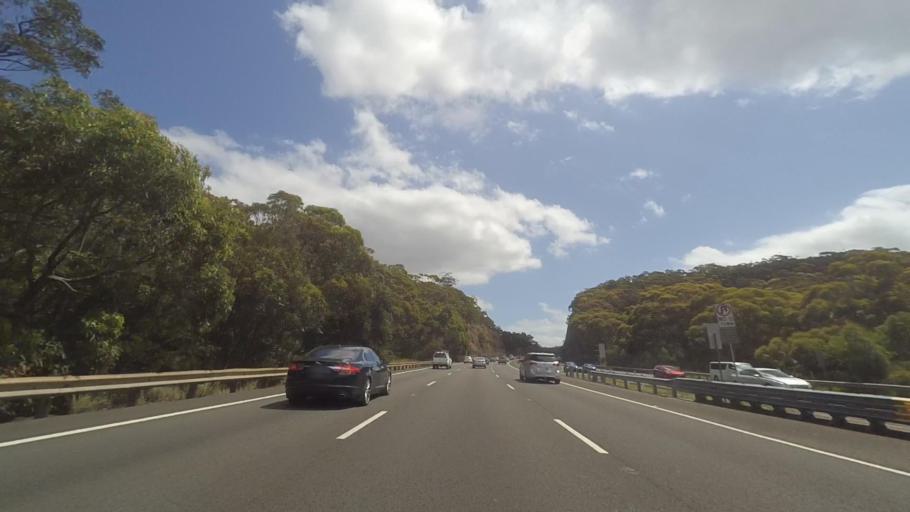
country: AU
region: New South Wales
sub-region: Hornsby Shire
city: Berowra
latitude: -33.5812
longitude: 151.1903
